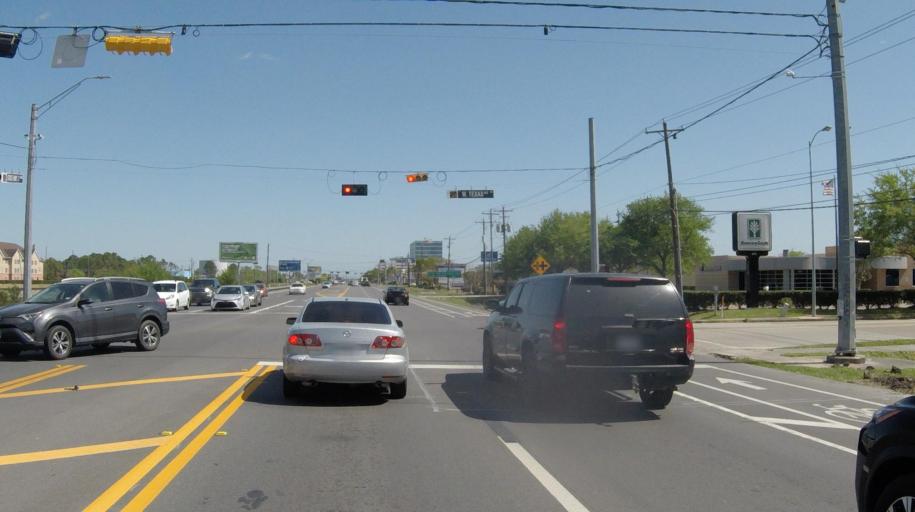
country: US
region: Texas
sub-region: Harris County
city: Webster
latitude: 29.5514
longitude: -95.1308
